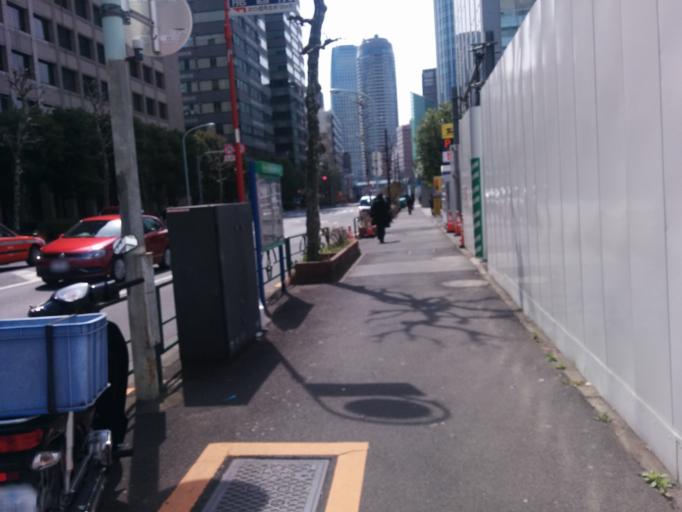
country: JP
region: Tokyo
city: Tokyo
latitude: 35.6688
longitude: 139.7510
